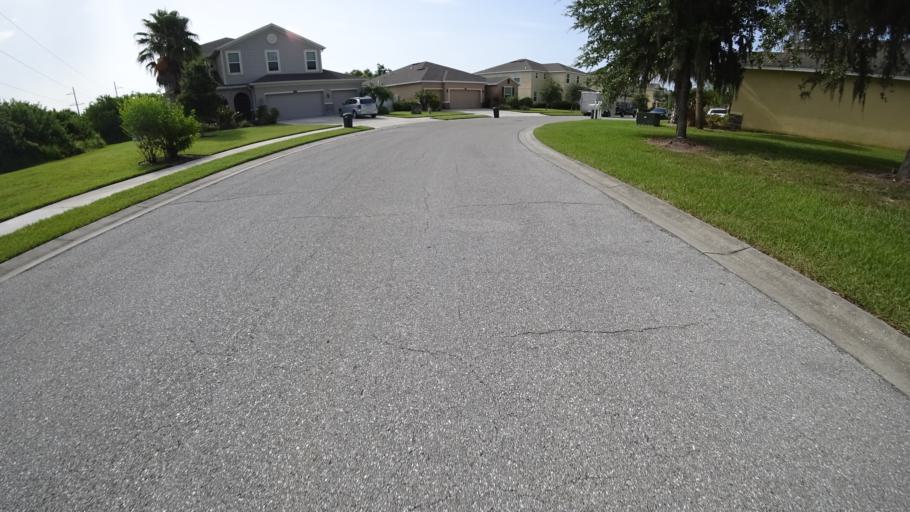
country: US
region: Florida
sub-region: Manatee County
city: Ellenton
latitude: 27.5519
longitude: -82.5072
